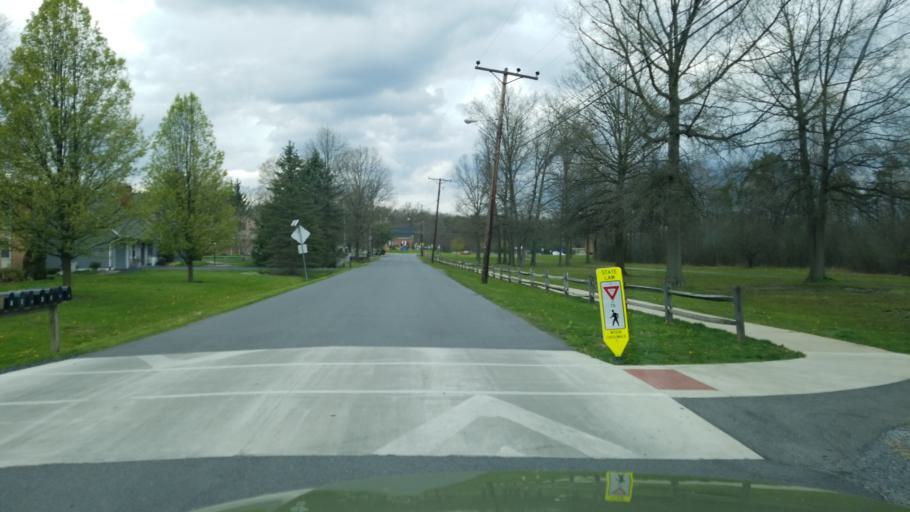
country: US
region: Pennsylvania
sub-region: Blair County
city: Hollidaysburg
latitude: 40.4382
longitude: -78.4001
